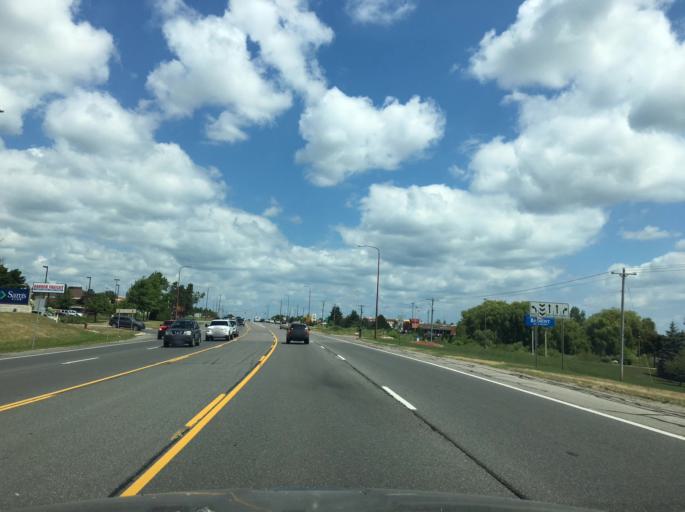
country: US
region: Michigan
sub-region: Grand Traverse County
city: Traverse City
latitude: 44.7193
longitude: -85.6460
